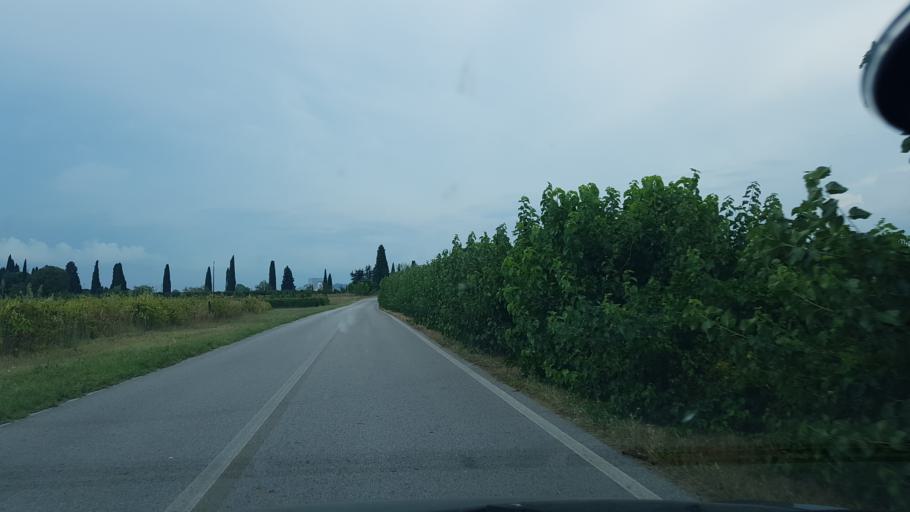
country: IT
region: Friuli Venezia Giulia
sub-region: Provincia di Gorizia
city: Farra d'Isonzo
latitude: 45.9023
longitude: 13.5134
